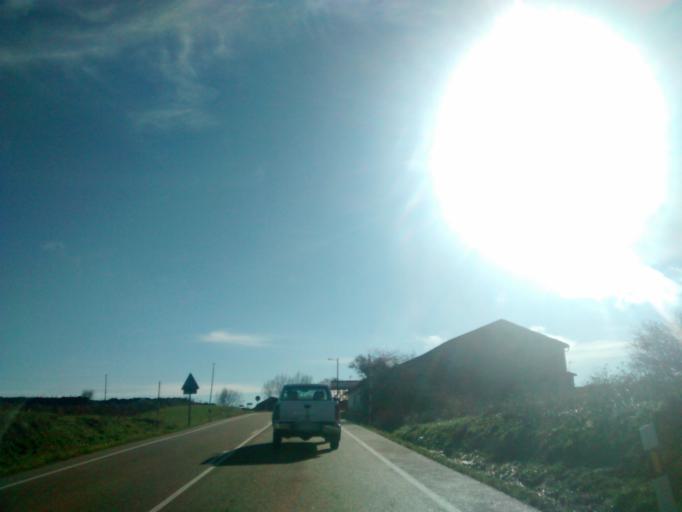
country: ES
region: Castille and Leon
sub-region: Provincia de Burgos
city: Arija
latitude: 43.0190
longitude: -3.8526
